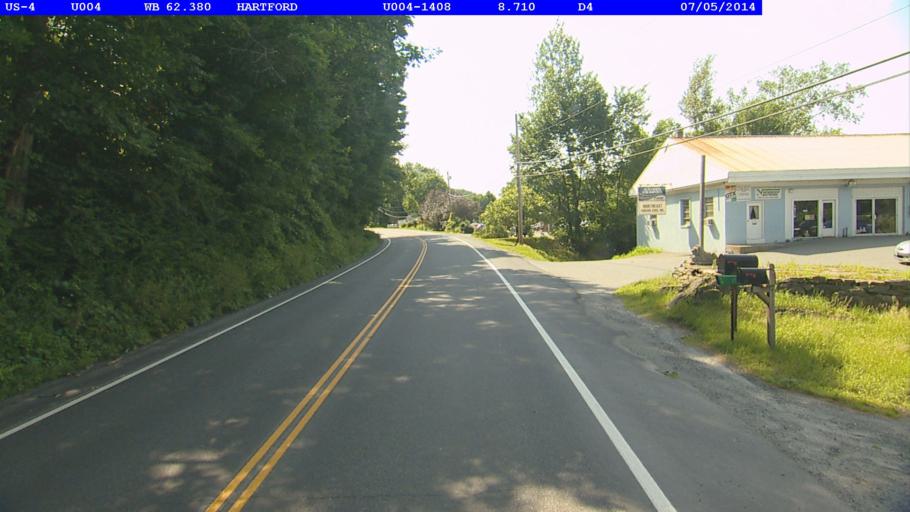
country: US
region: Vermont
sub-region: Windsor County
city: White River Junction
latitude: 43.6571
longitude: -72.3400
